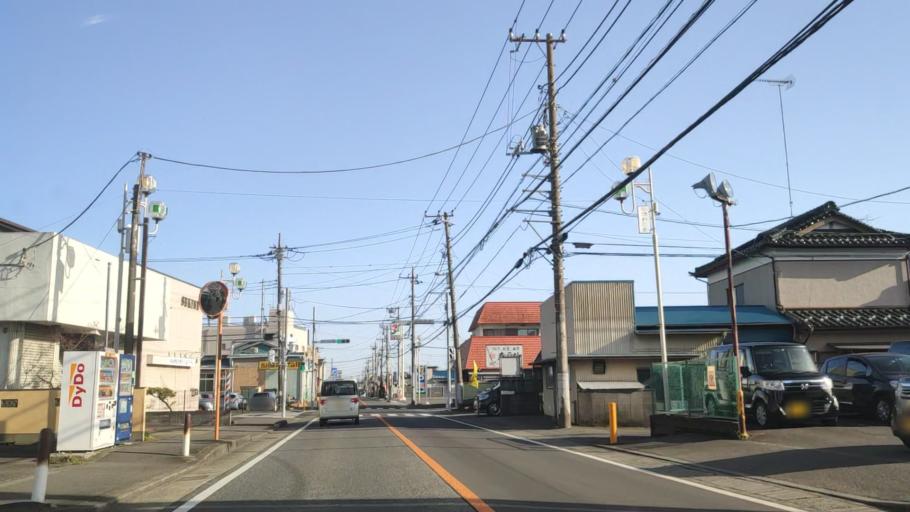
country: JP
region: Kanagawa
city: Zama
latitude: 35.5185
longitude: 139.3321
